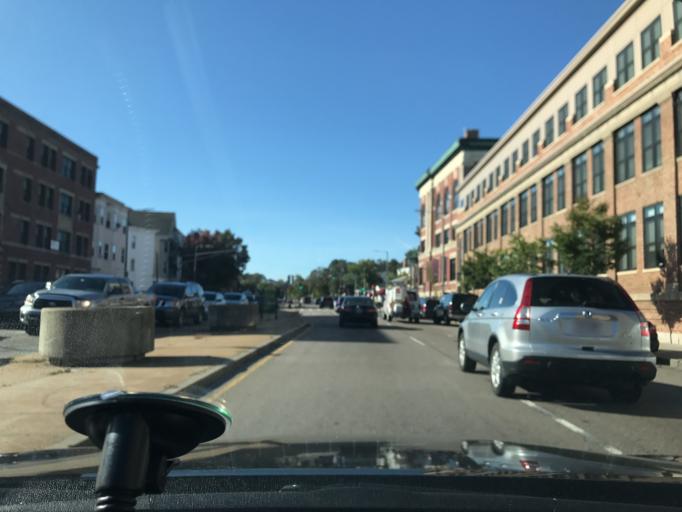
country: US
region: Massachusetts
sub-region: Suffolk County
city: South Boston
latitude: 42.3154
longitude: -71.0669
